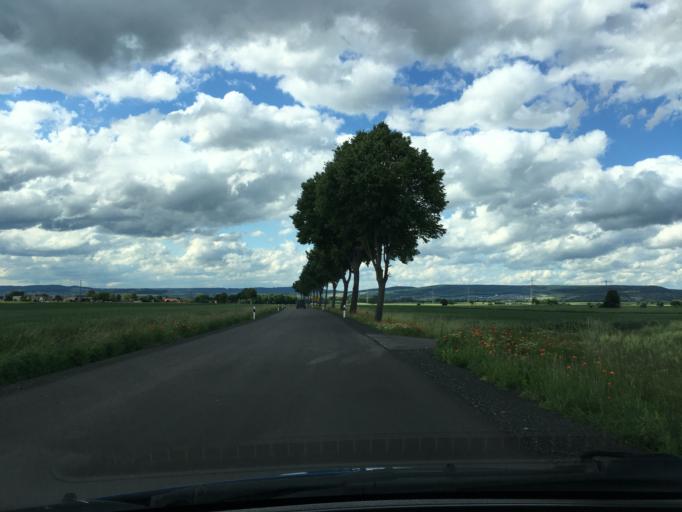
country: DE
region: Lower Saxony
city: Moringen
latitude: 51.7573
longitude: 9.8724
